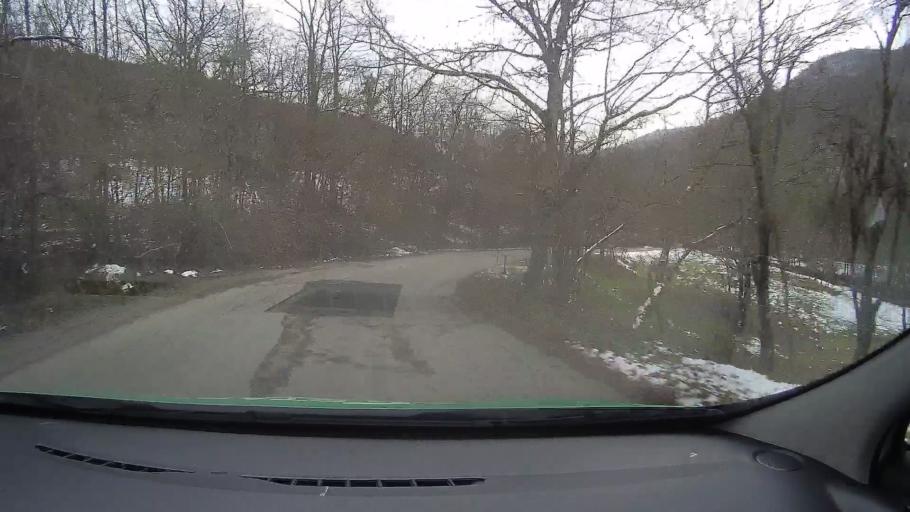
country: RO
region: Hunedoara
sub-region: Comuna Balsa
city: Balsa
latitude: 46.0146
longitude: 23.1497
